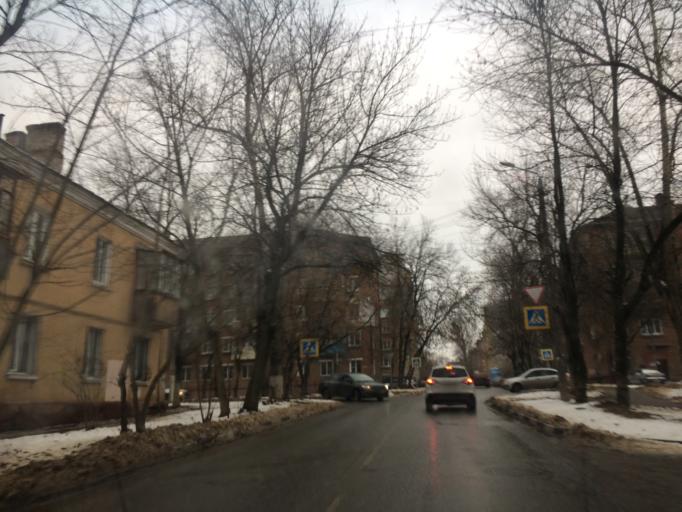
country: RU
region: Tula
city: Mendeleyevskiy
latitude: 54.1654
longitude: 37.5779
